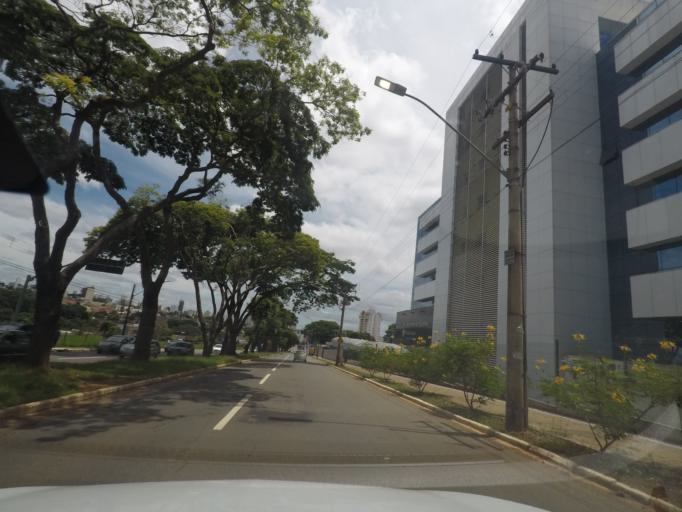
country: BR
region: Goias
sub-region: Goiania
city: Goiania
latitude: -16.6890
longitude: -49.2412
